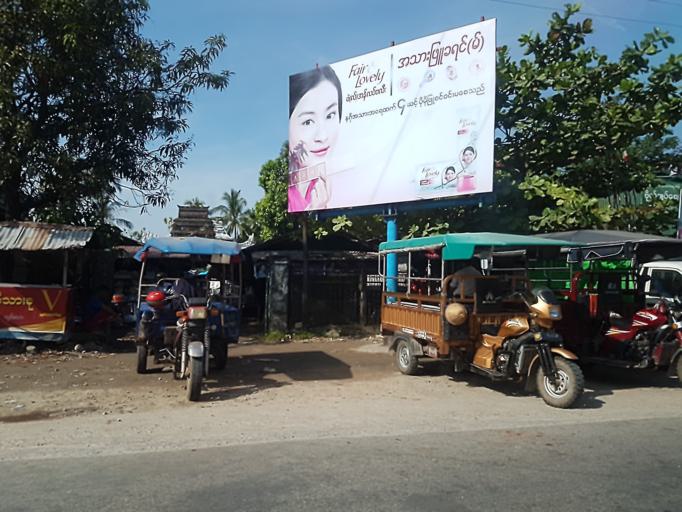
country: MM
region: Mon
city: Thaton
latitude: 16.6910
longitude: 97.4267
